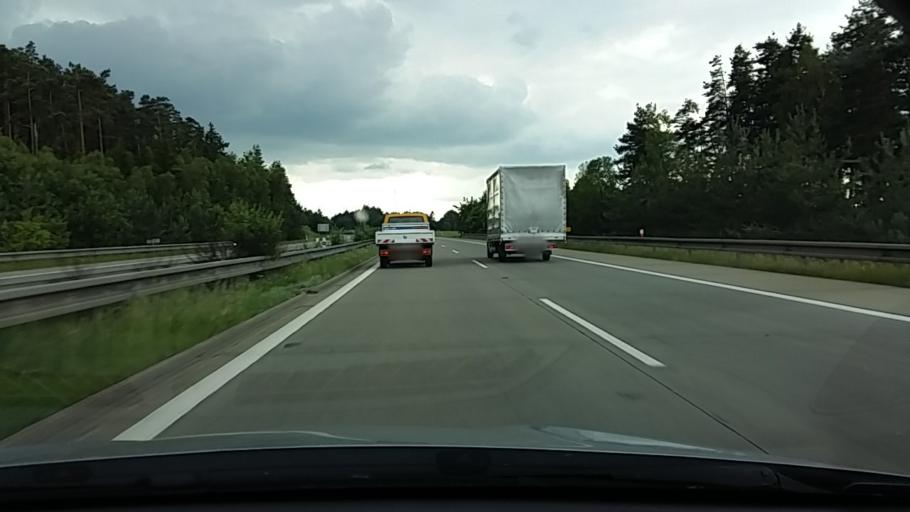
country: CZ
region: Plzensky
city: Bor
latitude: 49.7522
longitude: 12.8125
